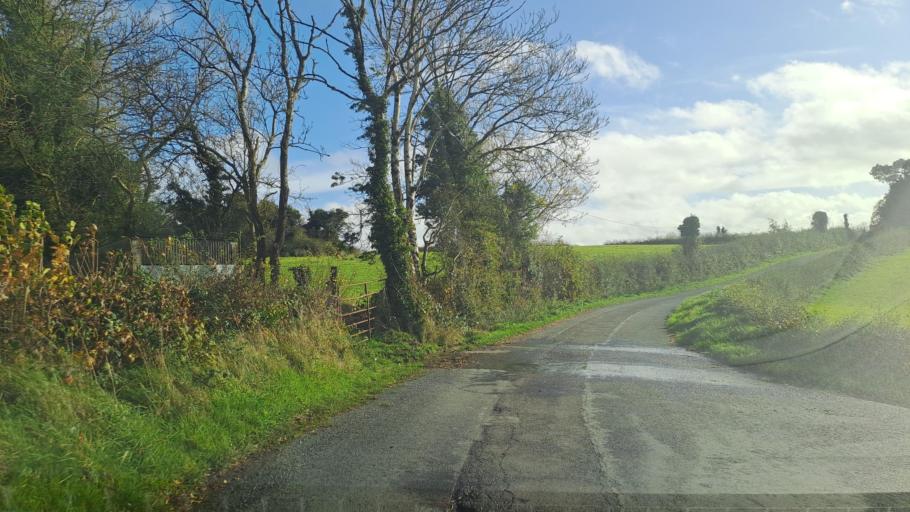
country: IE
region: Ulster
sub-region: An Cabhan
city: Cootehill
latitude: 54.0067
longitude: -7.0379
